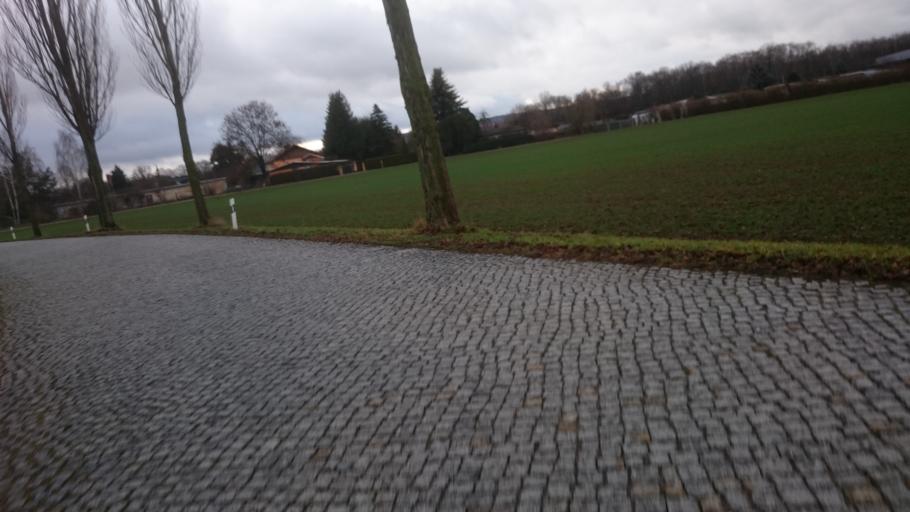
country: DE
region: Saxony
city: Zwickau
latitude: 50.7459
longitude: 12.4958
